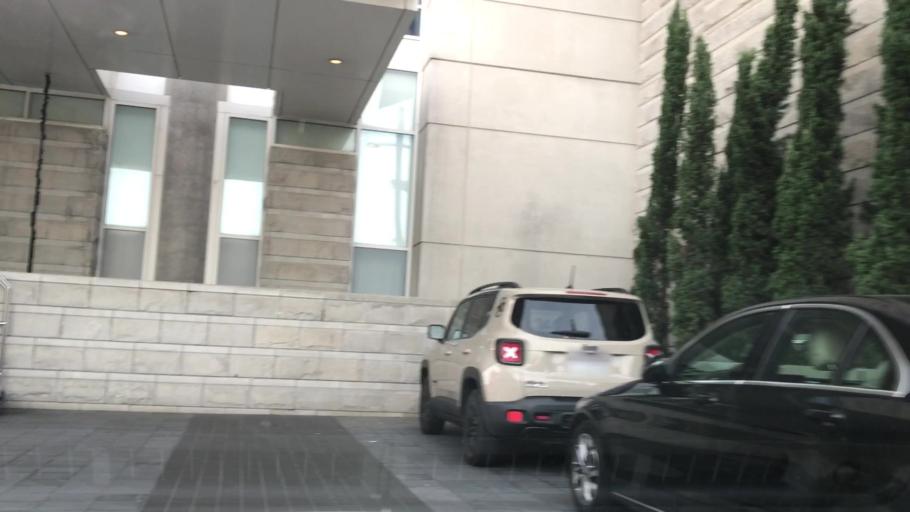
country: US
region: Texas
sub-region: Dallas County
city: Dallas
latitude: 32.7886
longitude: -96.8093
